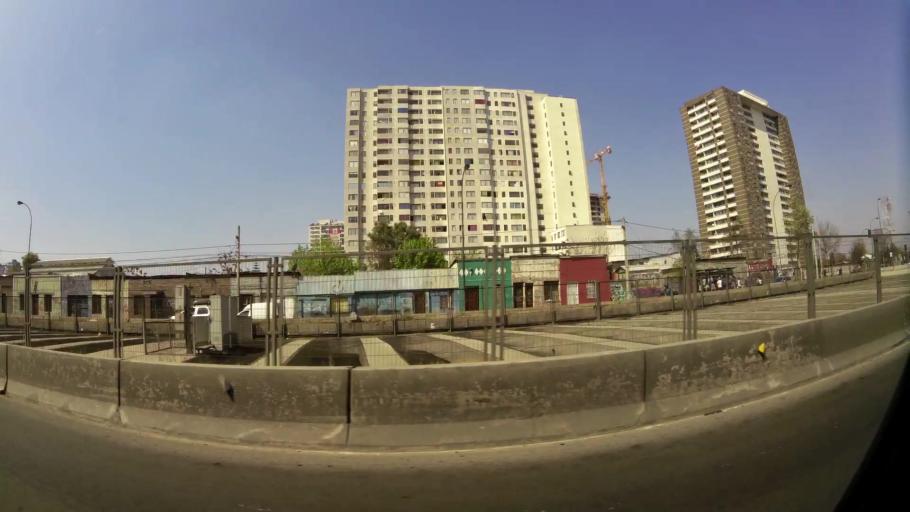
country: CL
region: Santiago Metropolitan
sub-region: Provincia de Santiago
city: Lo Prado
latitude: -33.4376
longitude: -70.6927
